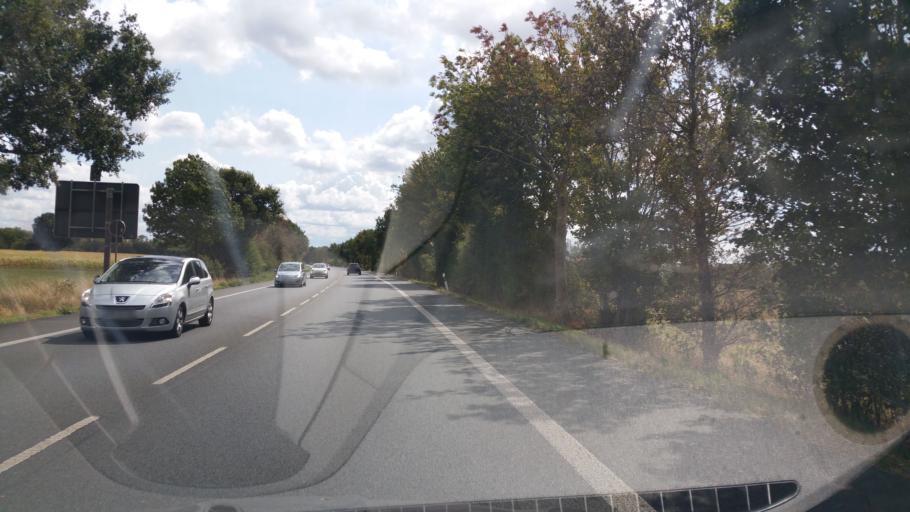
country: DE
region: North Rhine-Westphalia
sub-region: Regierungsbezirk Dusseldorf
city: Hamminkeln
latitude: 51.7653
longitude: 6.5822
